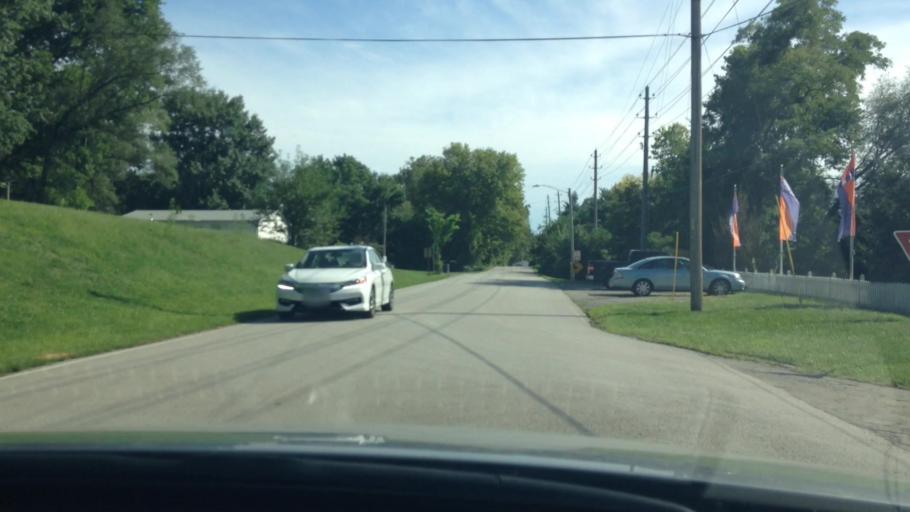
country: US
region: Missouri
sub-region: Platte County
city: Weatherby Lake
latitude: 39.3157
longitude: -94.6664
